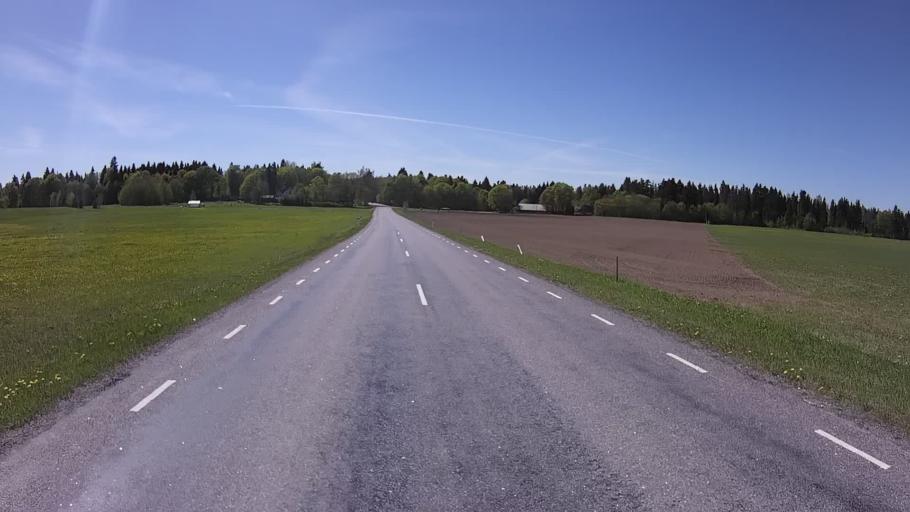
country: EE
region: Harju
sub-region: Rae vald
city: Vaida
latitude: 59.0616
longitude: 25.1443
